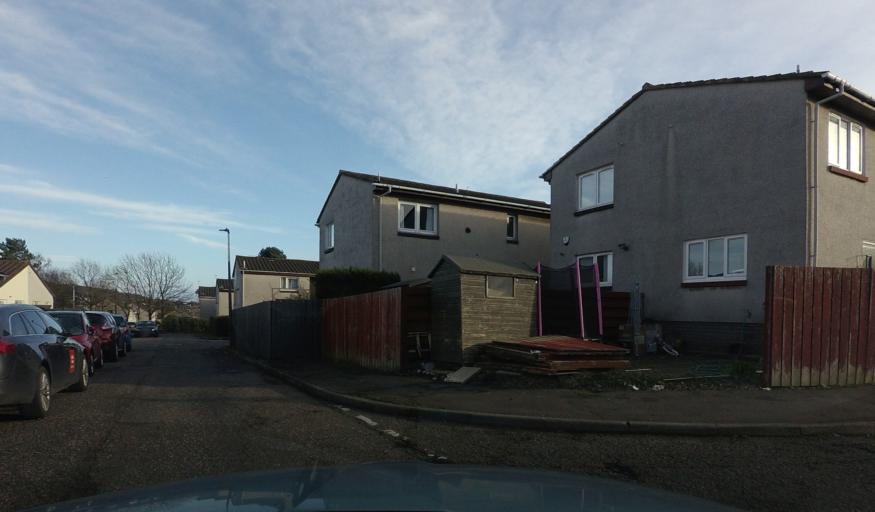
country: GB
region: Scotland
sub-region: Edinburgh
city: Currie
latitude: 55.9465
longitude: -3.3067
